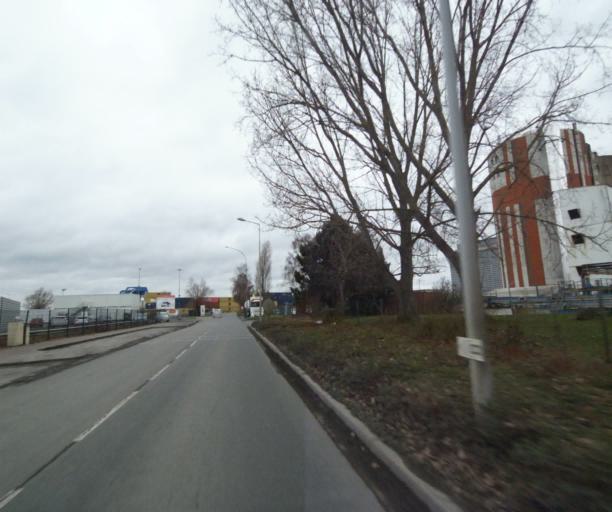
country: FR
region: Nord-Pas-de-Calais
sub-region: Departement du Nord
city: Bruay-sur-l'Escaut
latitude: 50.3905
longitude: 3.5500
